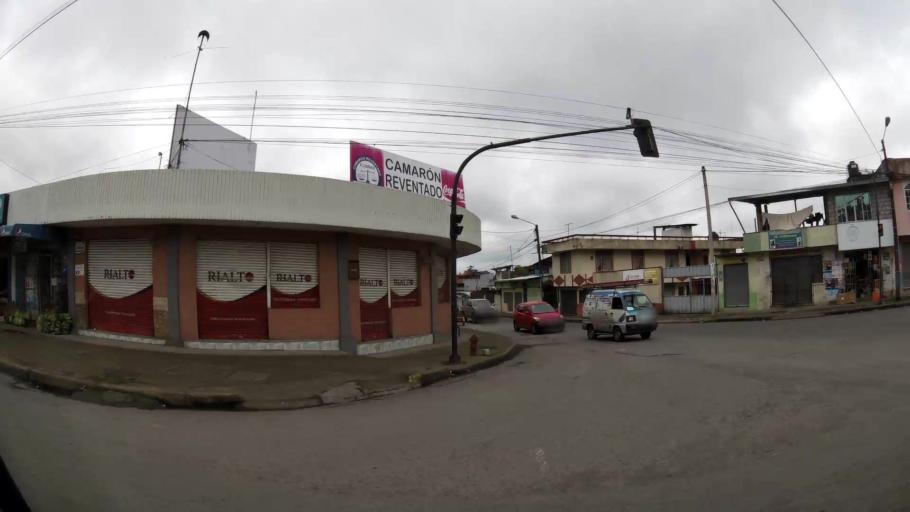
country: EC
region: Santo Domingo de los Tsachilas
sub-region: Canton Santo Domingo de los Colorados
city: Santo Domingo de los Colorados
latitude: -0.2633
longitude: -79.1634
